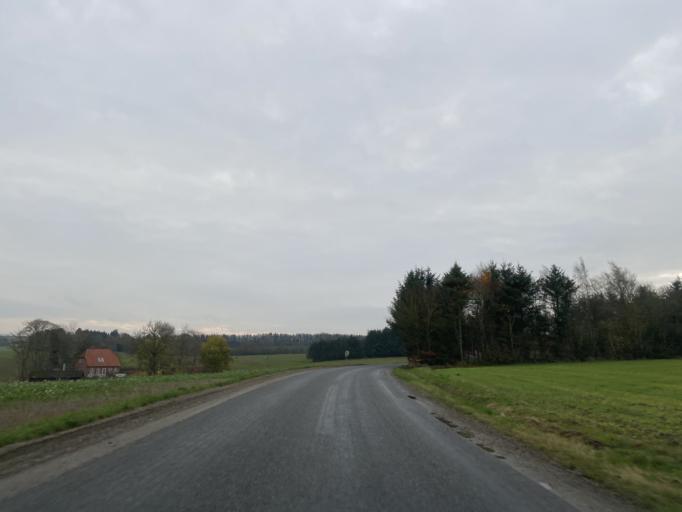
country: DK
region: Central Jutland
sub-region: Skanderborg Kommune
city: Ry
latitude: 56.1411
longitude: 9.7121
